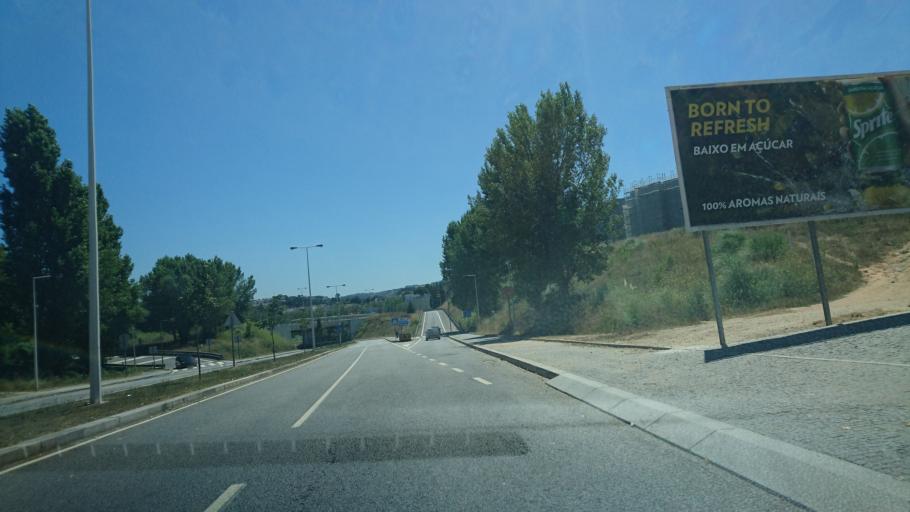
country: PT
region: Porto
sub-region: Gondomar
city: Valbom
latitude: 41.1581
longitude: -8.5722
